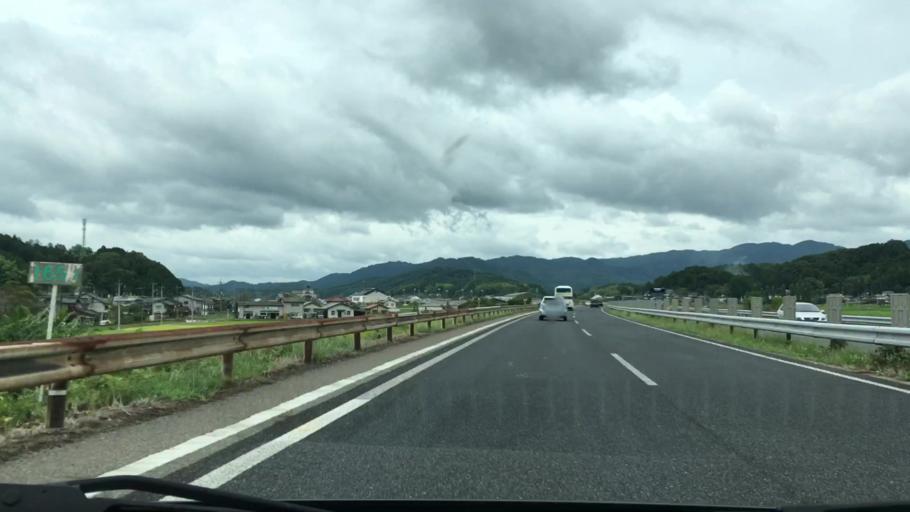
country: JP
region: Okayama
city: Tsuyama
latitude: 35.0577
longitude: 133.9118
